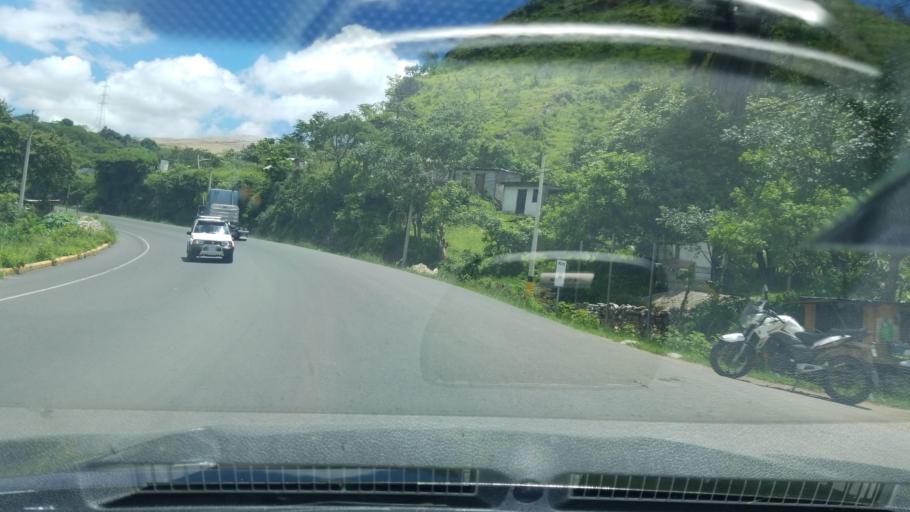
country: HN
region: Francisco Morazan
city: Rio Abajo
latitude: 14.1500
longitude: -87.2130
